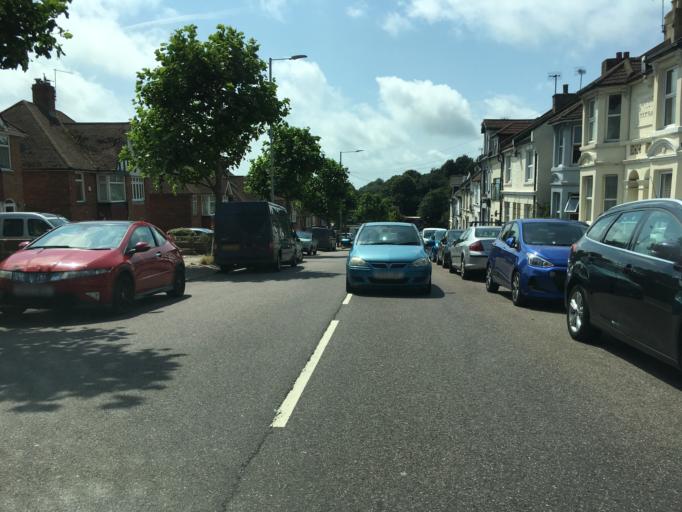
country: GB
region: England
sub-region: East Sussex
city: Hastings
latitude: 50.8666
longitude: 0.5994
